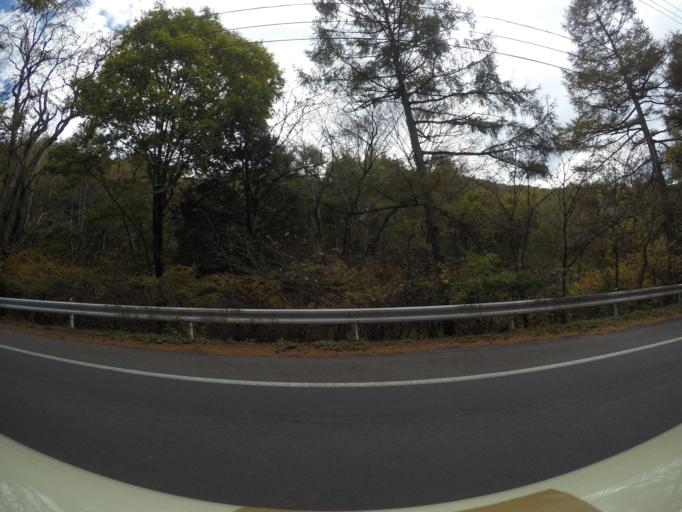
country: JP
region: Nagano
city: Chino
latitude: 35.9649
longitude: 138.1177
